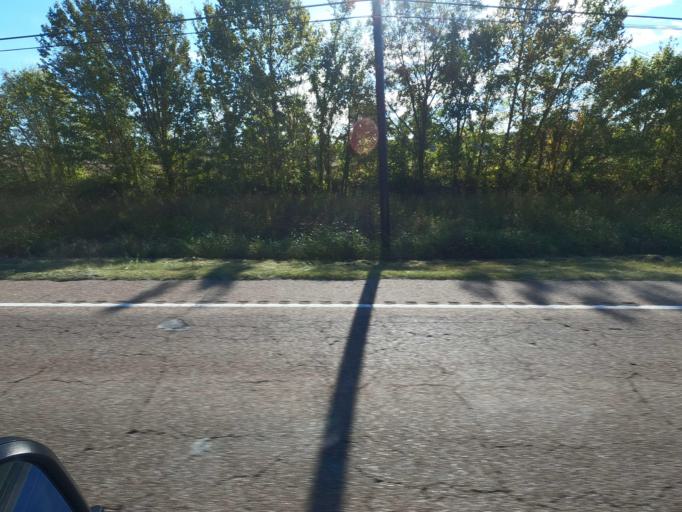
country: US
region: Tennessee
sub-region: Tipton County
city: Brighton
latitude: 35.5077
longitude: -89.7122
